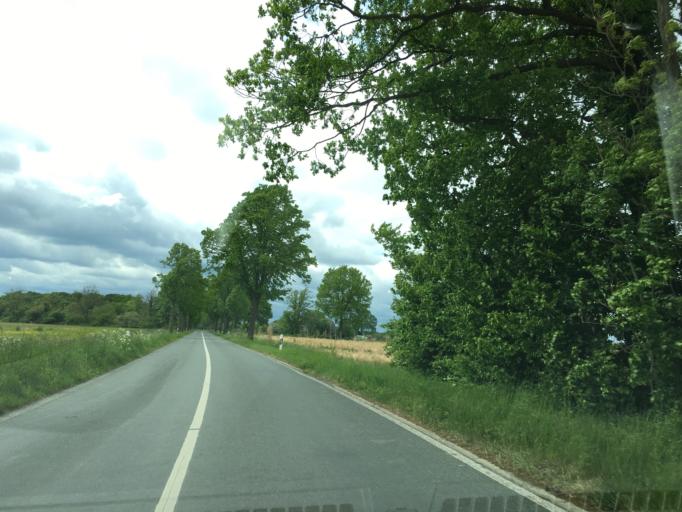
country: DE
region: North Rhine-Westphalia
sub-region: Regierungsbezirk Munster
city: Altenberge
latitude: 51.9883
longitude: 7.5019
